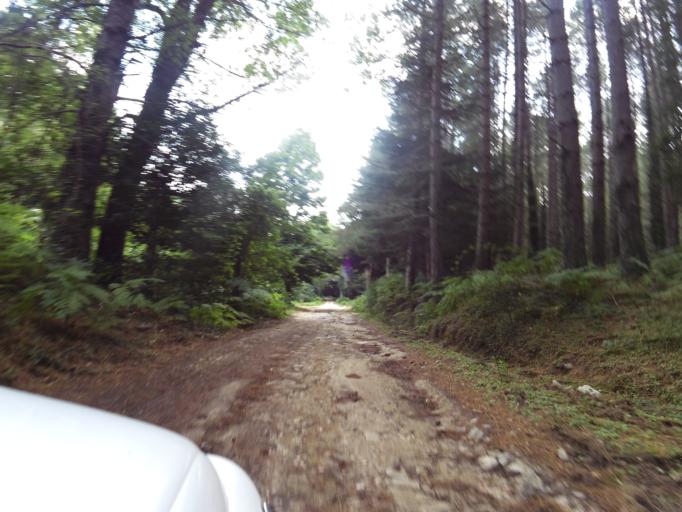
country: IT
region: Calabria
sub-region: Provincia di Vibo-Valentia
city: Nardodipace
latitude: 38.5149
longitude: 16.3789
